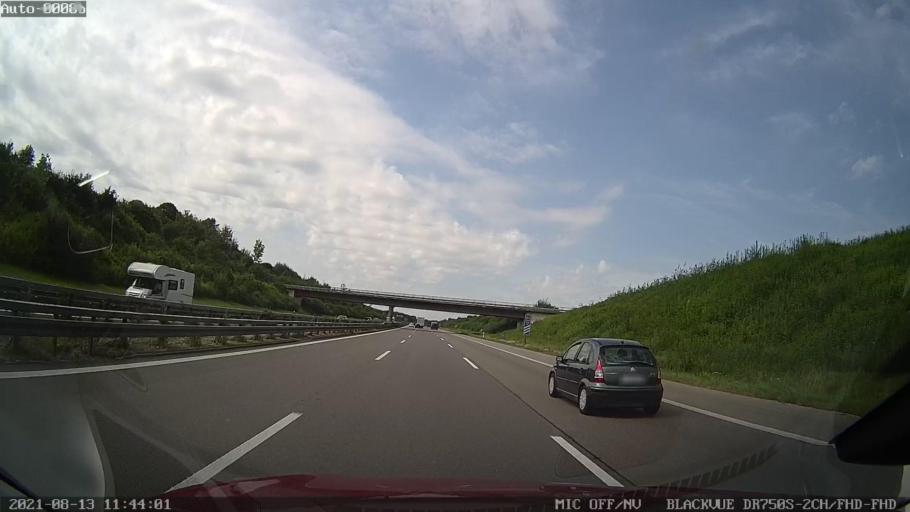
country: DE
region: Baden-Wuerttemberg
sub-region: Tuebingen Region
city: Langenau
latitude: 48.4612
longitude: 10.0860
